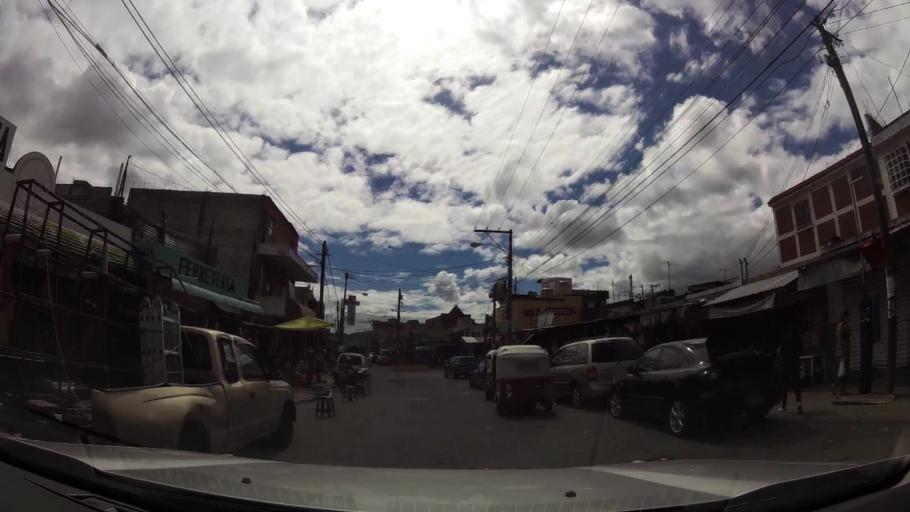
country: GT
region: Guatemala
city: Guatemala City
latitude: 14.6821
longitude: -90.5463
